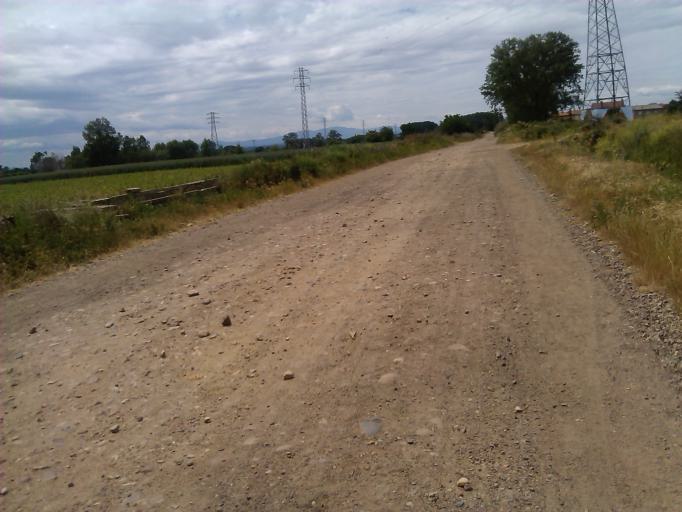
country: ES
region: Castille and Leon
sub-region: Provincia de Leon
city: Bustillo del Paramo
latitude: 42.4601
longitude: -5.8313
